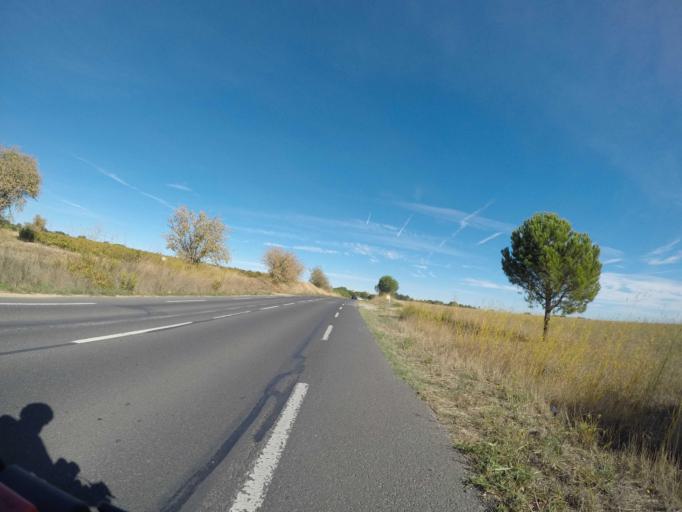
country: FR
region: Languedoc-Roussillon
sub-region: Departement des Pyrenees-Orientales
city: Ponteilla
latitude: 42.6199
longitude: 2.8111
